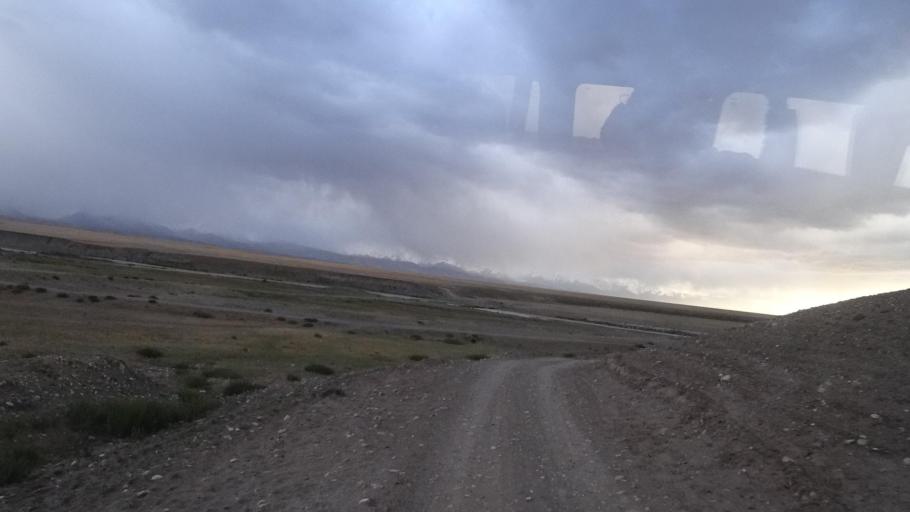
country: KG
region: Osh
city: Osh
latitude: 39.6597
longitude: 72.8797
